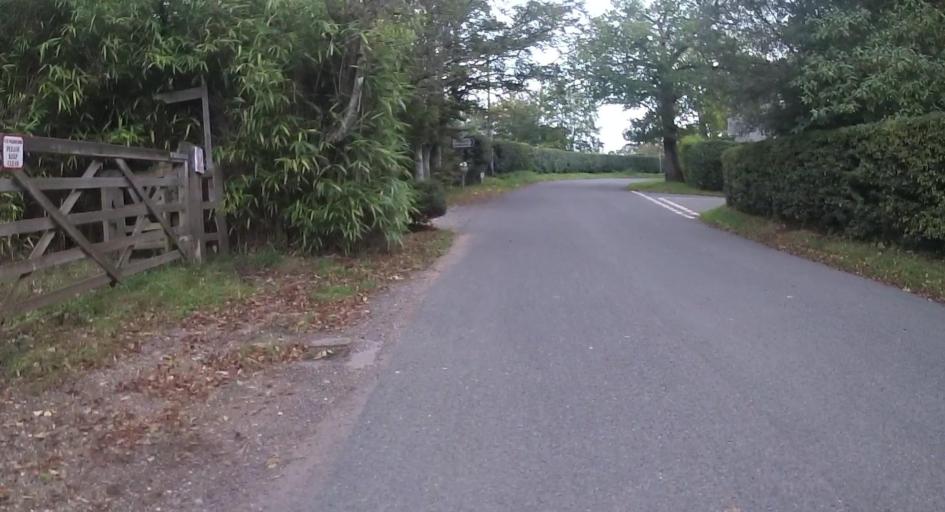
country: GB
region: England
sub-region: Hampshire
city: Hook
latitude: 51.3128
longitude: -0.9349
